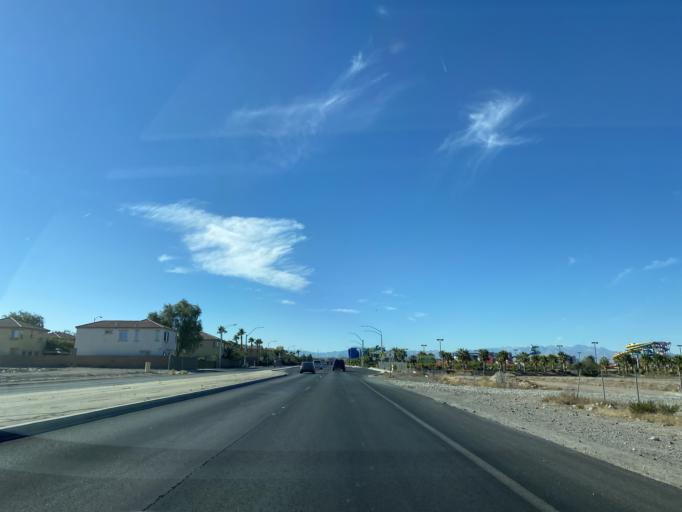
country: US
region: Nevada
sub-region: Clark County
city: Henderson
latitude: 36.0711
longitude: -115.0201
